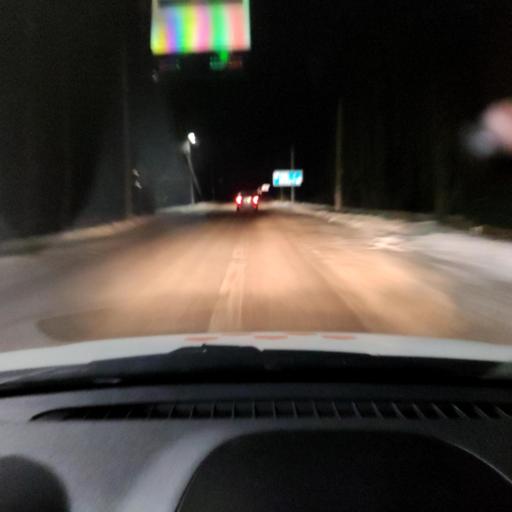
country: RU
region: Tatarstan
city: Vysokaya Gora
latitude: 55.8031
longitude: 49.3768
